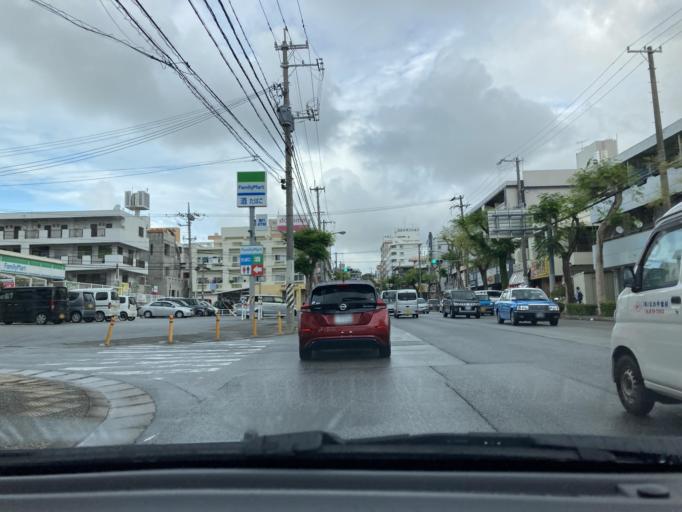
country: JP
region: Okinawa
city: Tomigusuku
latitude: 26.1970
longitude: 127.6959
